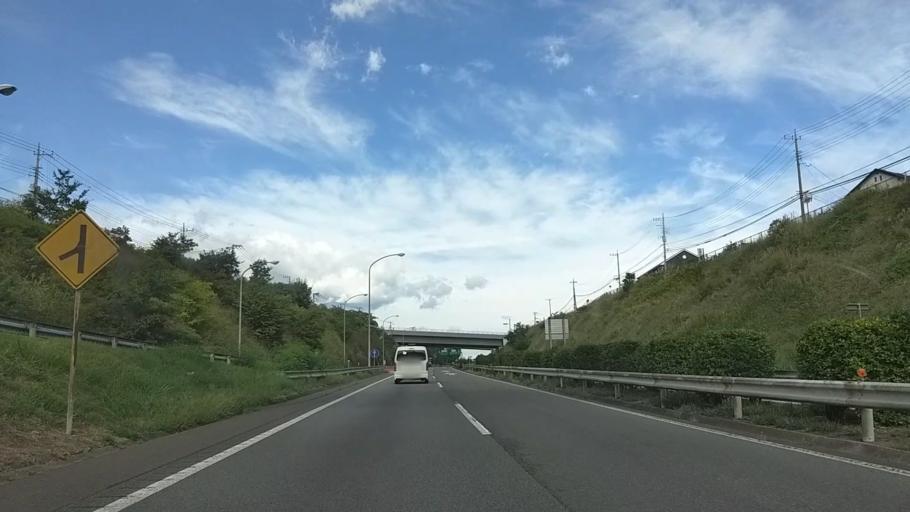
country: JP
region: Yamanashi
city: Ryuo
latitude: 35.6796
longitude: 138.5078
